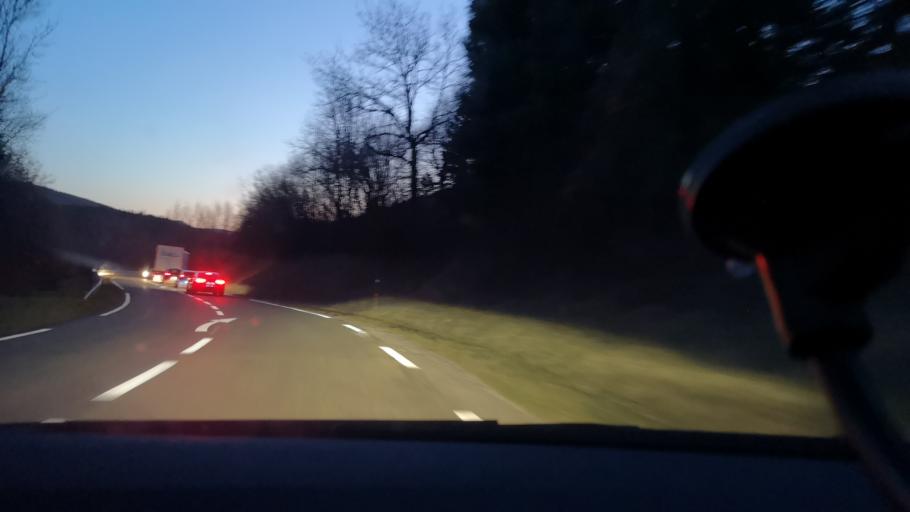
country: FR
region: Franche-Comte
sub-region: Departement du Jura
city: Champagnole
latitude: 46.7540
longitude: 5.9335
